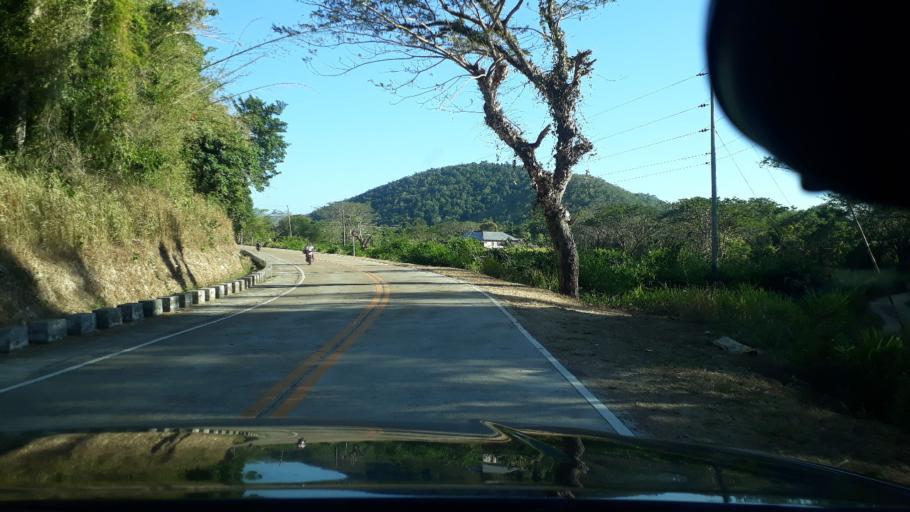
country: PH
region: Mimaropa
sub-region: Province of Palawan
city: Coron
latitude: 12.0425
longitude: 120.1556
